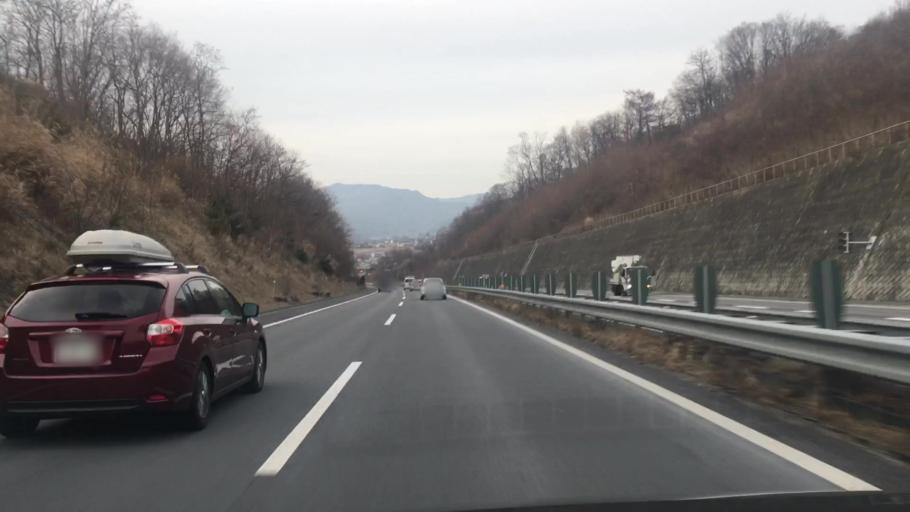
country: JP
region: Nagano
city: Ueda
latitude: 36.4010
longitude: 138.3121
